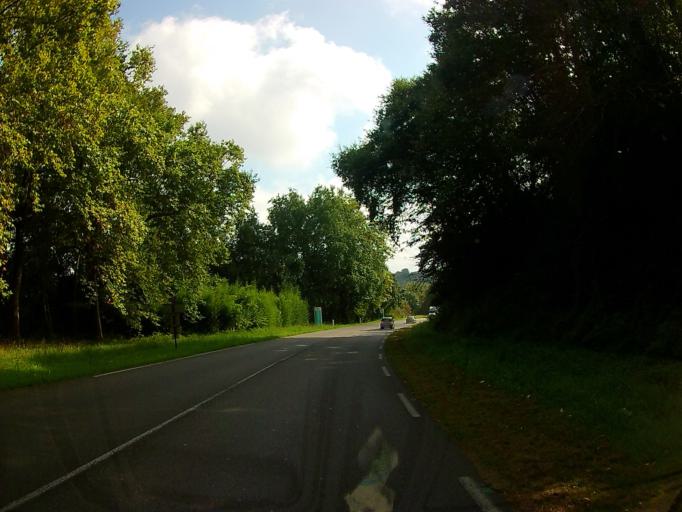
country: FR
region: Aquitaine
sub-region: Departement des Pyrenees-Atlantiques
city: Boucau
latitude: 43.5202
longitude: -1.4642
